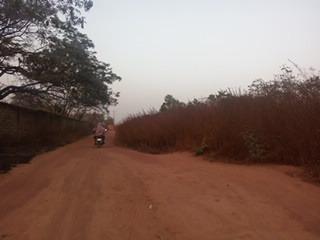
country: BJ
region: Borgou
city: Parakou
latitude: 9.3314
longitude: 2.5984
